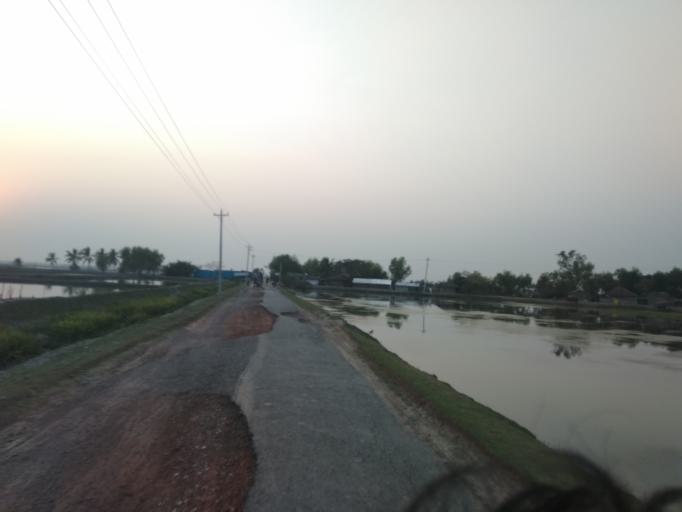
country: IN
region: West Bengal
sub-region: North 24 Parganas
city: Taki
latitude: 22.4562
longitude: 89.0747
